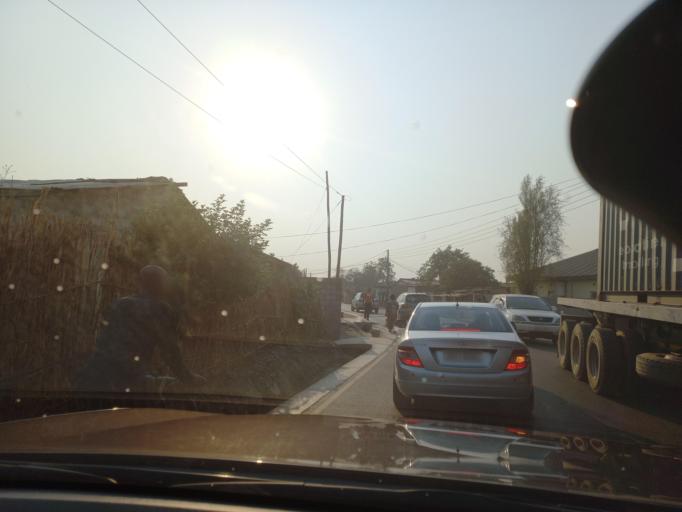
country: ZM
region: Lusaka
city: Lusaka
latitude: -15.4031
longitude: 28.3405
